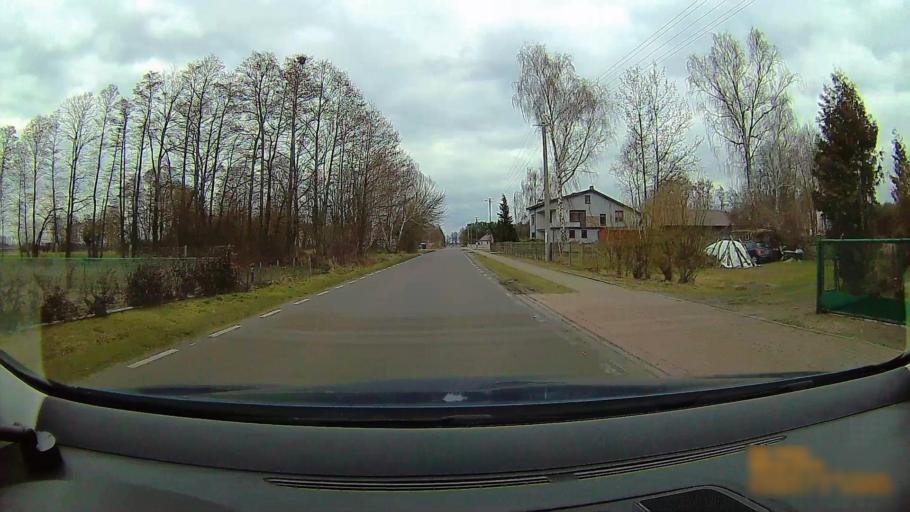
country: PL
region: Greater Poland Voivodeship
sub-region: Powiat koninski
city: Rzgow Pierwszy
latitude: 52.1034
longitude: 18.0929
